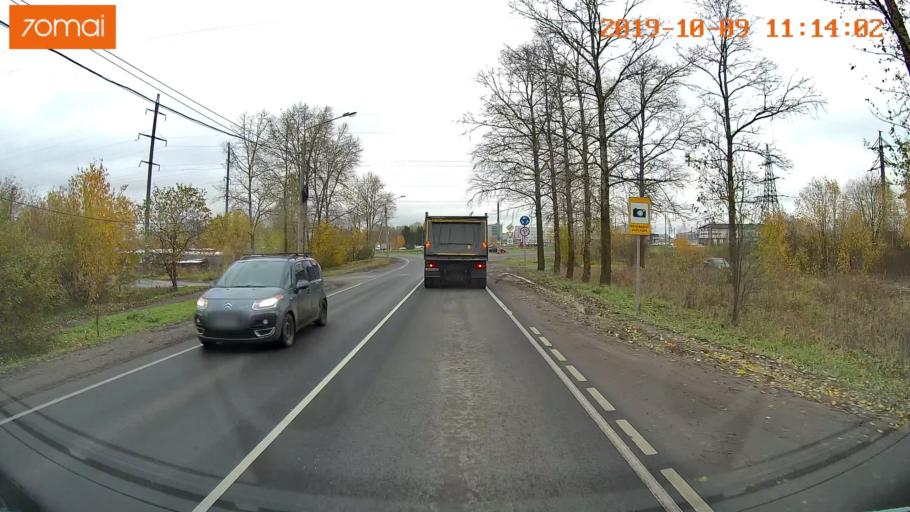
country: RU
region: Vologda
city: Vologda
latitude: 59.1857
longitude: 39.8494
